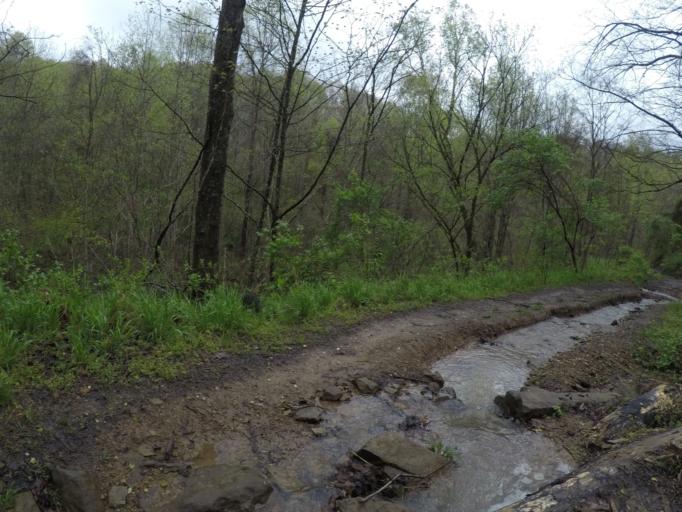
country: US
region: Ohio
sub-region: Lawrence County
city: Burlington
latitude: 38.3832
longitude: -82.4867
